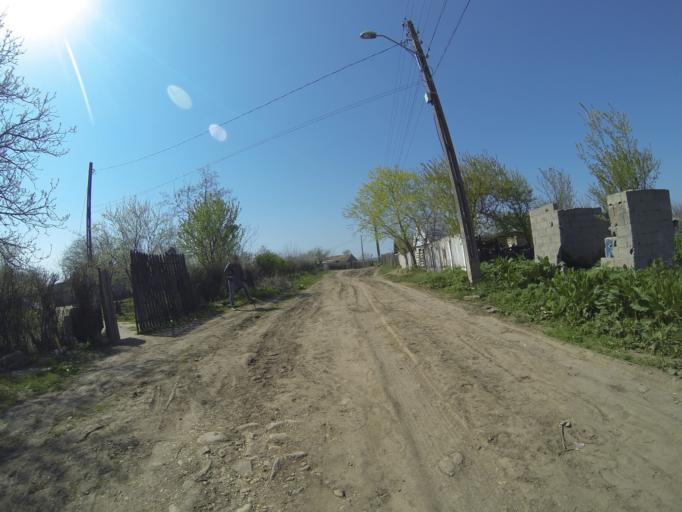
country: RO
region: Dolj
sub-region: Comuna Segarcea
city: Segarcea
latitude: 44.0927
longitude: 23.7298
